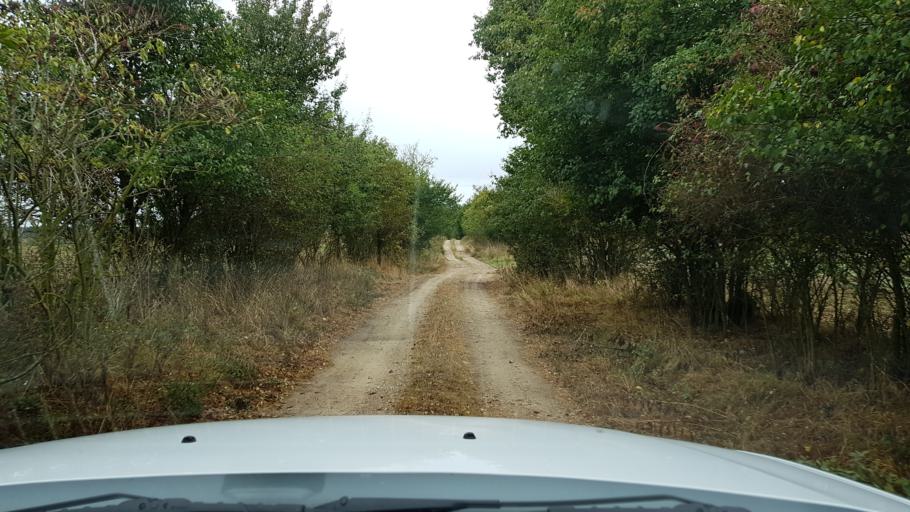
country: PL
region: West Pomeranian Voivodeship
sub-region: Powiat gryfinski
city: Chojna
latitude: 52.9009
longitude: 14.4478
